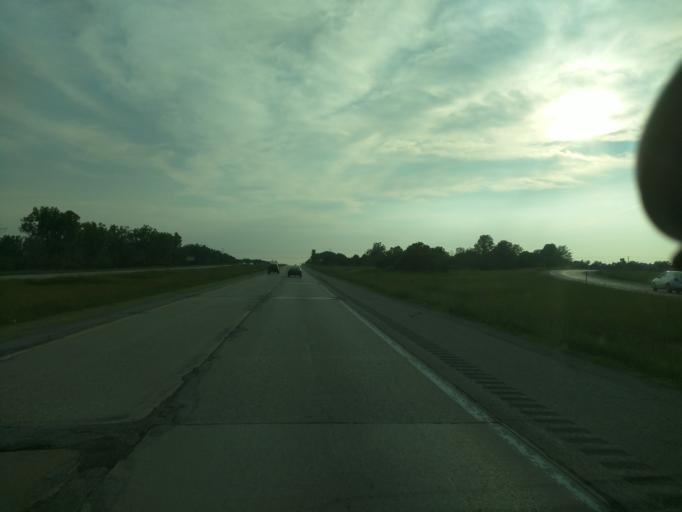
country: US
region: Michigan
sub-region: Ingham County
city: Edgemont Park
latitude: 42.7224
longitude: -84.5979
